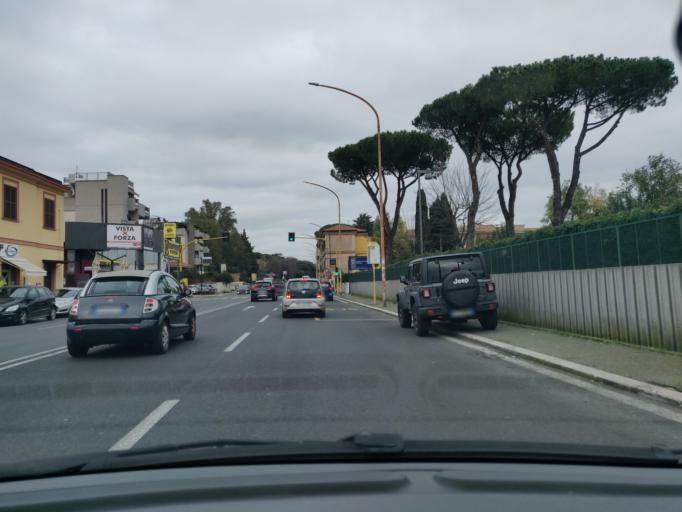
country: VA
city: Vatican City
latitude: 41.8960
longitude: 12.4192
